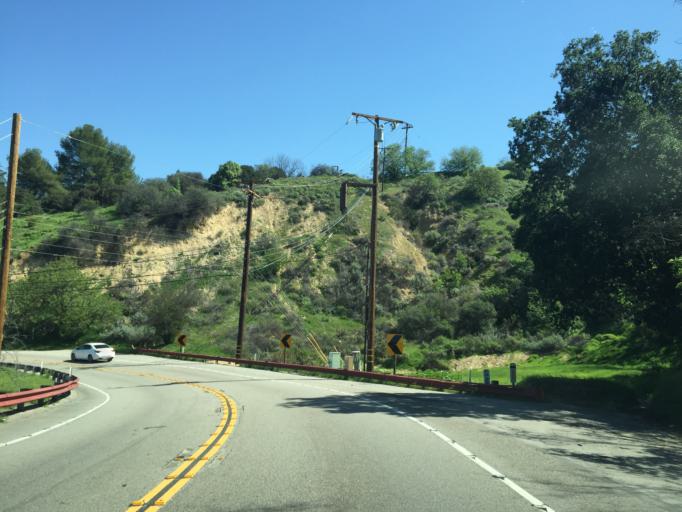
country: US
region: California
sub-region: Los Angeles County
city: Woodland Hills
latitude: 34.1415
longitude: -118.6058
